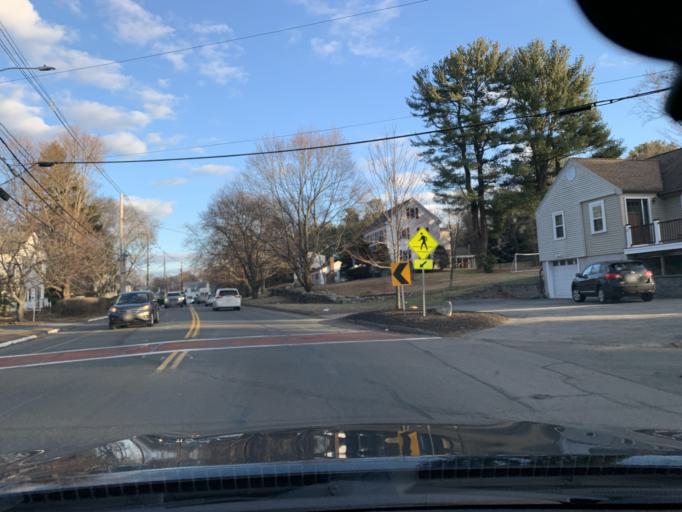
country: US
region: Massachusetts
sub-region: Essex County
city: Danvers
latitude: 42.5746
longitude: -70.9570
